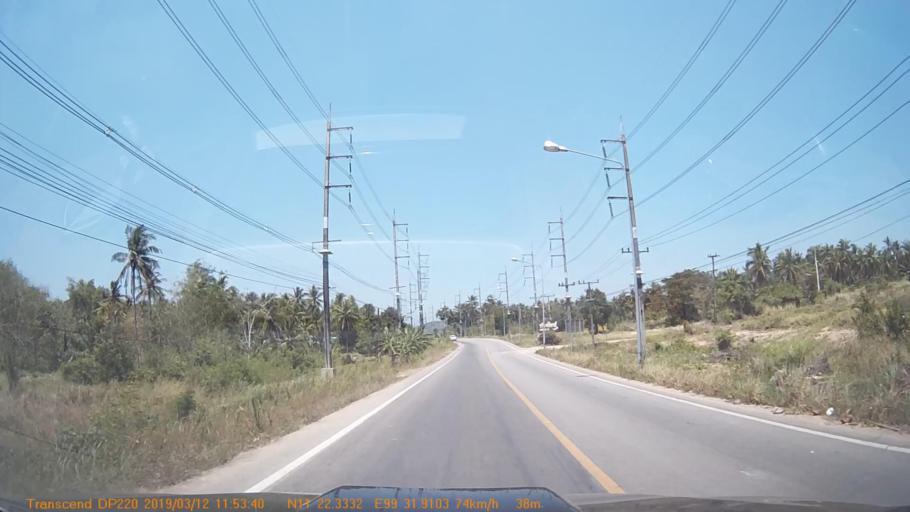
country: TH
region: Prachuap Khiri Khan
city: Thap Sakae
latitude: 11.3723
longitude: 99.5318
